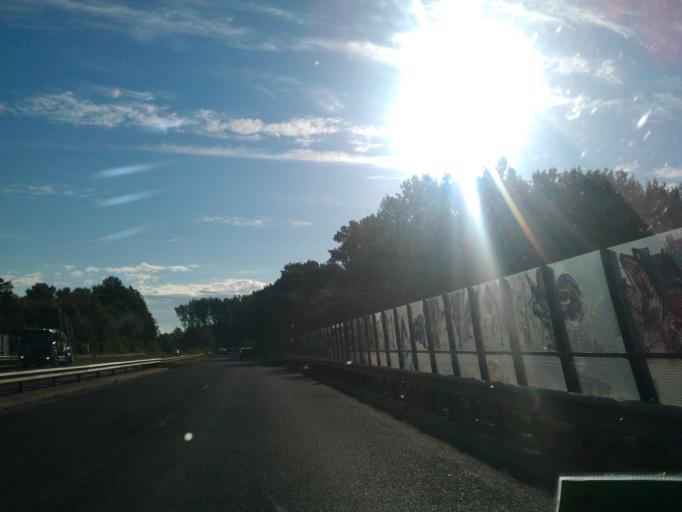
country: DE
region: North Rhine-Westphalia
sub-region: Regierungsbezirk Koln
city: Aachen
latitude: 50.7925
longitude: 6.0664
